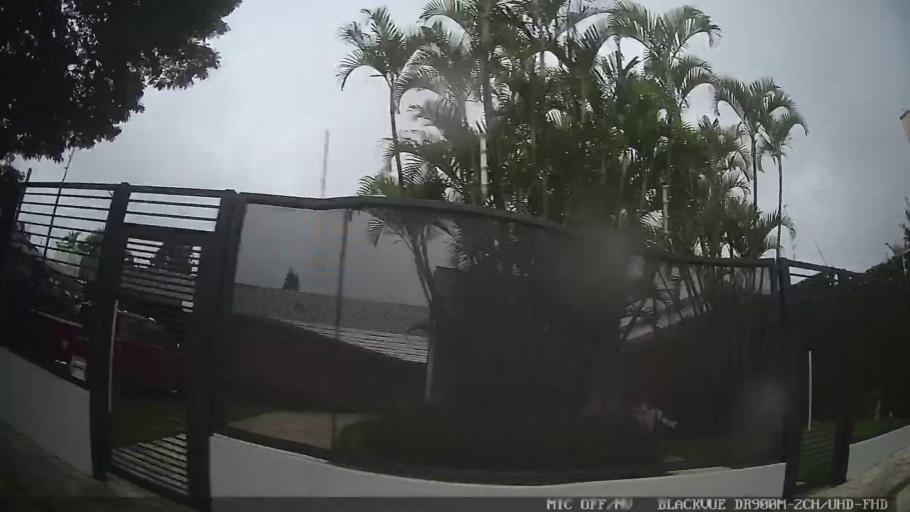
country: BR
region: Sao Paulo
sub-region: Mogi das Cruzes
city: Mogi das Cruzes
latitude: -23.5241
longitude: -46.1775
